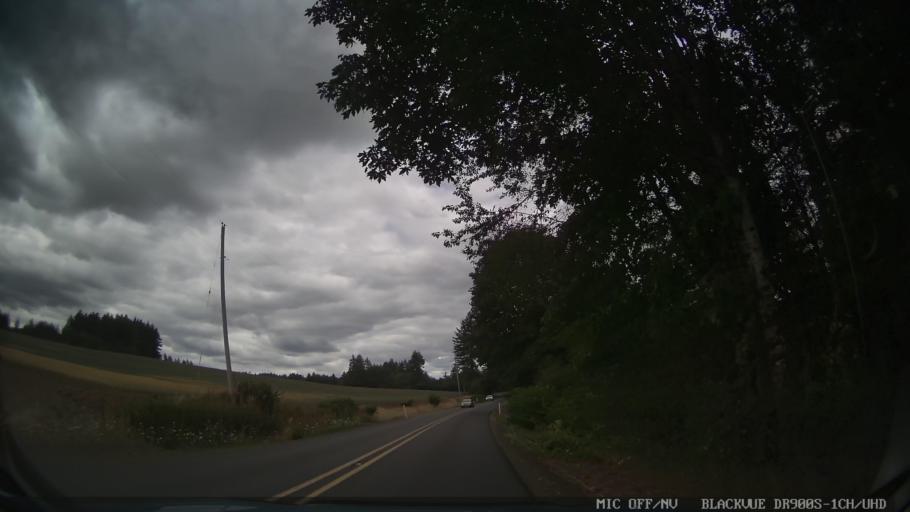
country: US
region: Oregon
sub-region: Linn County
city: Lyons
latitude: 44.8506
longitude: -122.6761
